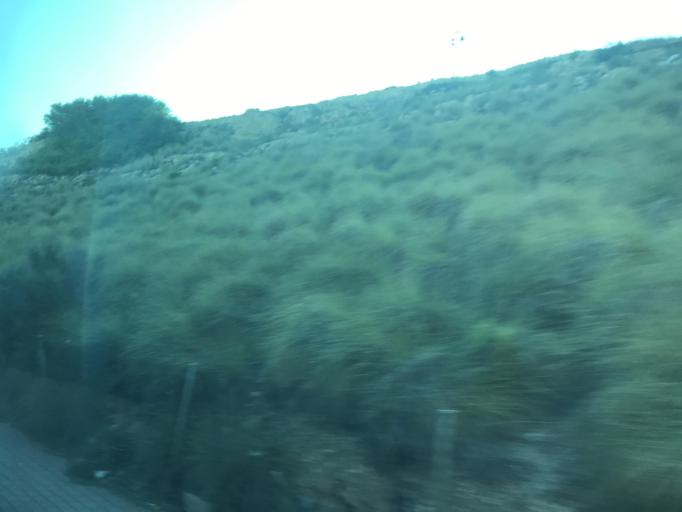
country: ES
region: Valencia
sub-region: Provincia de Alicante
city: Torrevieja
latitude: 38.0010
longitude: -0.6505
